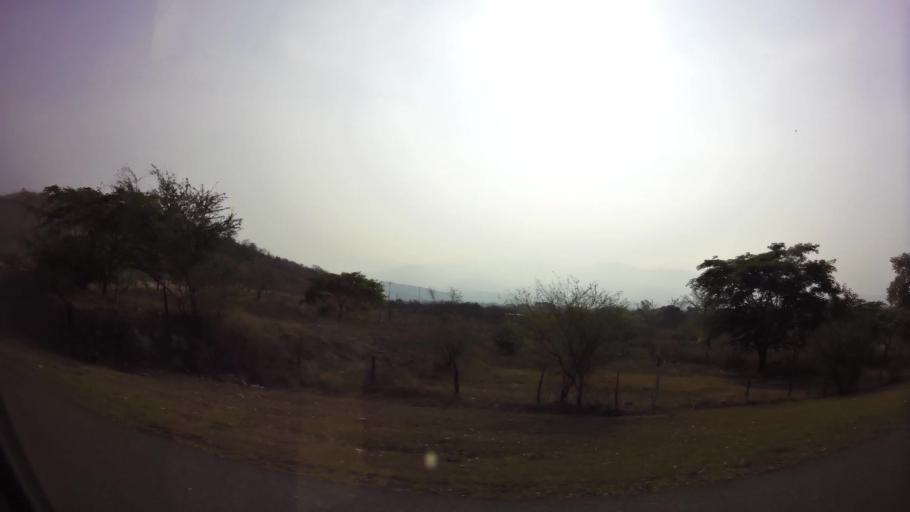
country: HN
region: Comayagua
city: Comayagua
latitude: 14.4498
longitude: -87.6629
